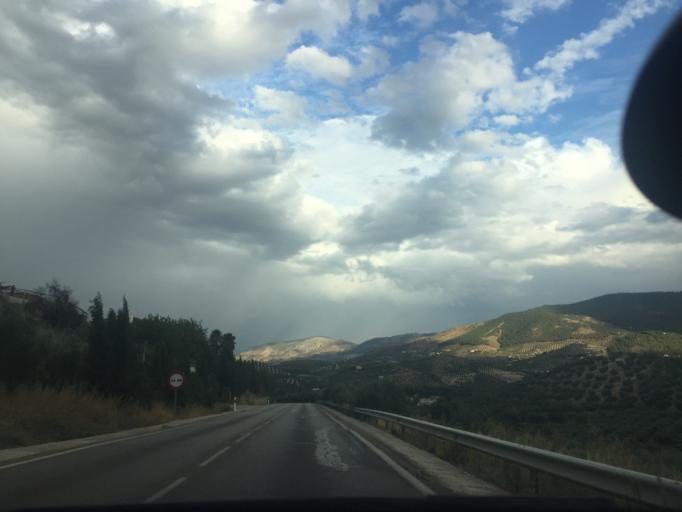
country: ES
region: Andalusia
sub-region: Provincia de Jaen
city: Jaen
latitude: 37.7608
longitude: -3.7641
